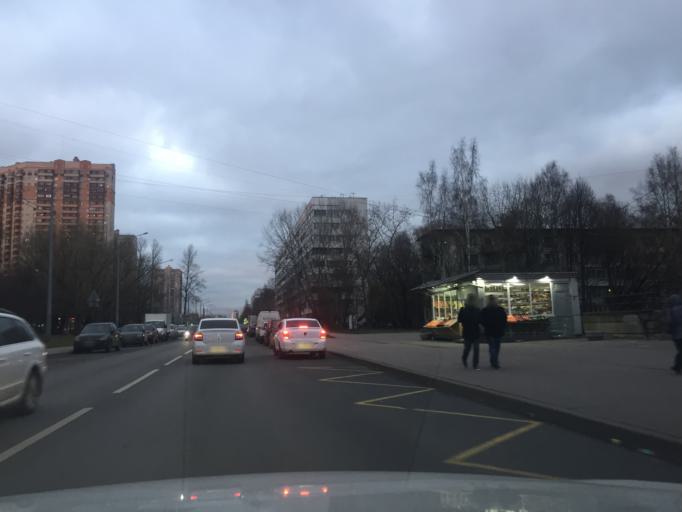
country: RU
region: St.-Petersburg
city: Grazhdanka
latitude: 60.0292
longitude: 30.4049
